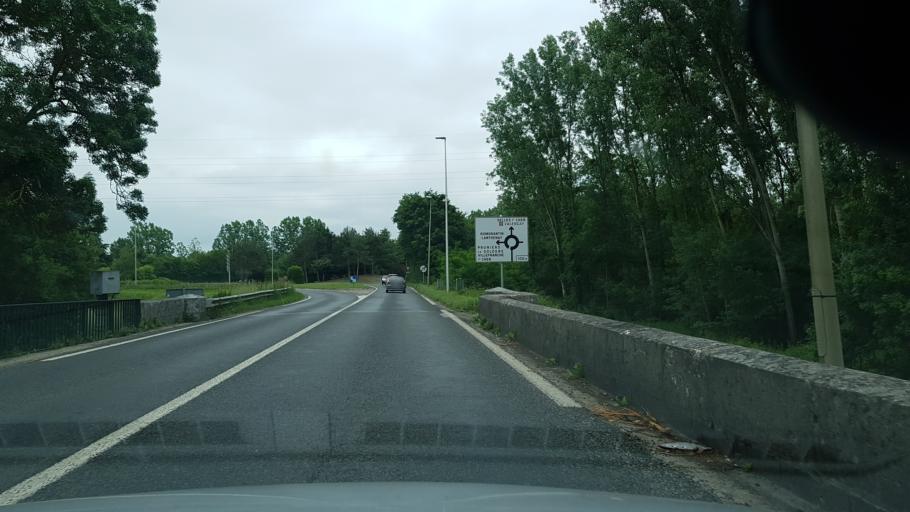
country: FR
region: Centre
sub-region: Departement du Loir-et-Cher
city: Selles-sur-Cher
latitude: 47.2872
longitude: 1.5352
